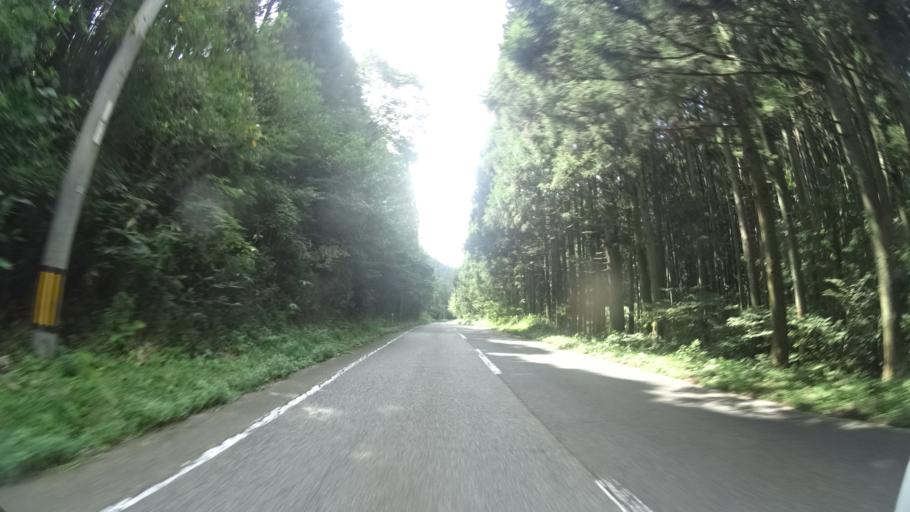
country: JP
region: Yamaguchi
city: Hagi
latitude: 34.5111
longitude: 131.5926
